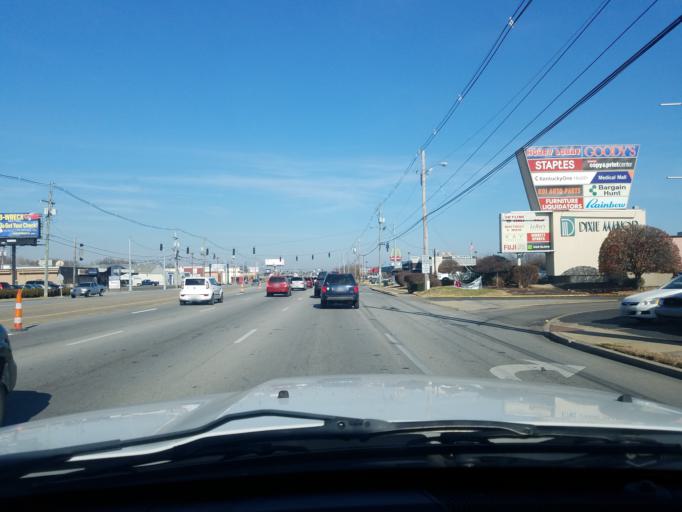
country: US
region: Kentucky
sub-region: Jefferson County
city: Pleasure Ridge Park
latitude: 38.1512
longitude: -85.8365
